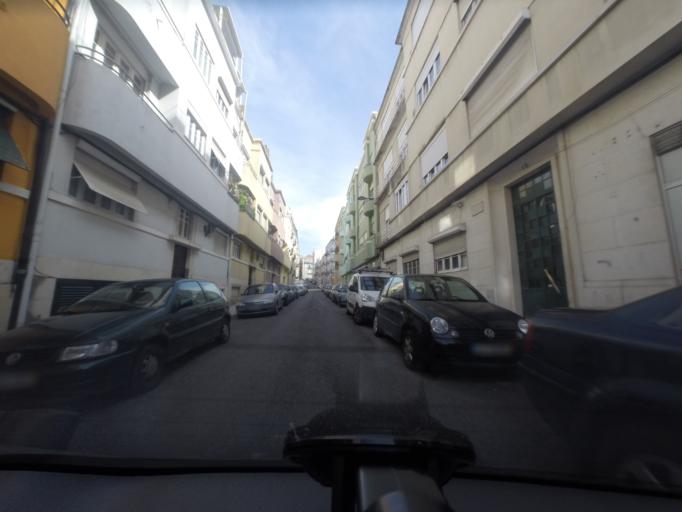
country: PT
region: Lisbon
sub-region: Lisbon
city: Lisbon
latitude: 38.7271
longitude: -9.1323
